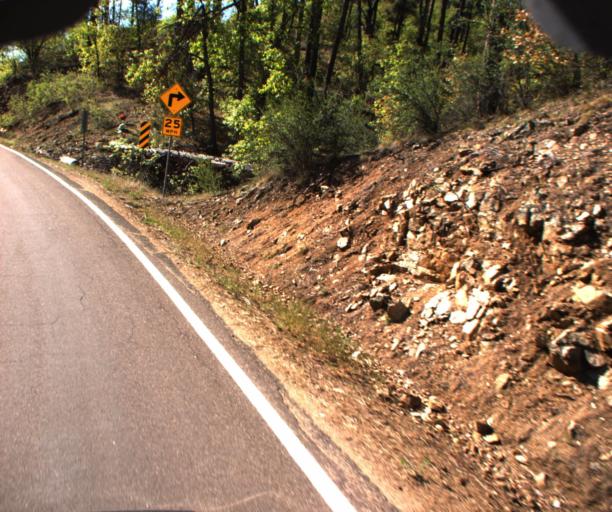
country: US
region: Arizona
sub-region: Yavapai County
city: Prescott
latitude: 34.4827
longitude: -112.5035
